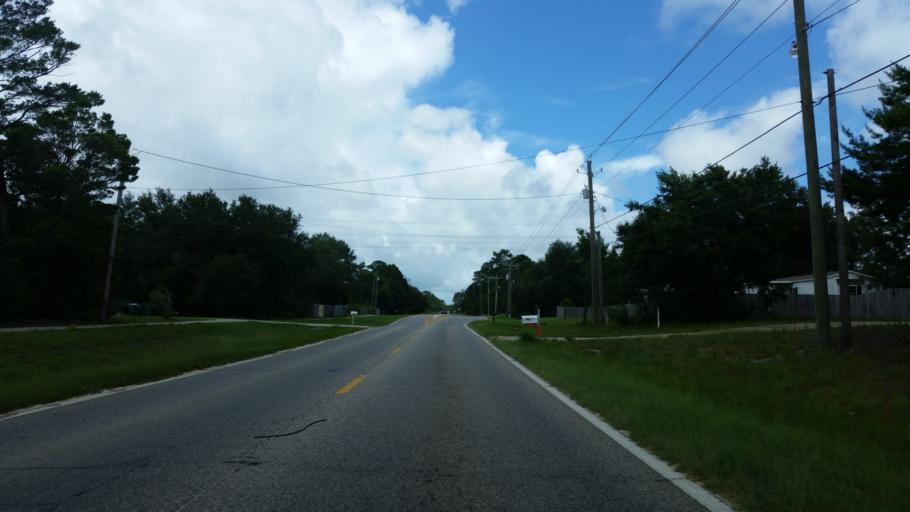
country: US
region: Florida
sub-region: Santa Rosa County
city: Holley
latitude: 30.4461
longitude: -86.9390
